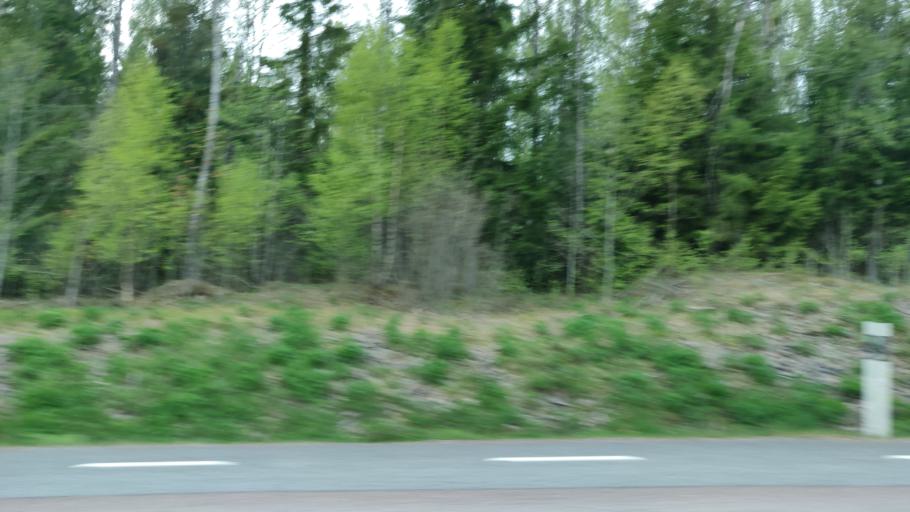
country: SE
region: Vaermland
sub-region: Forshaga Kommun
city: Deje
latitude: 59.6810
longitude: 13.4362
